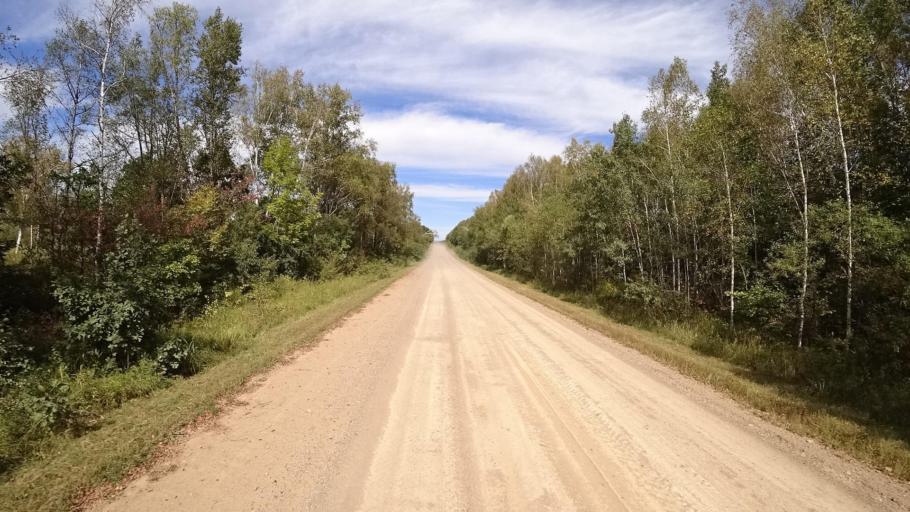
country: RU
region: Primorskiy
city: Yakovlevka
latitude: 44.6864
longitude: 133.6180
